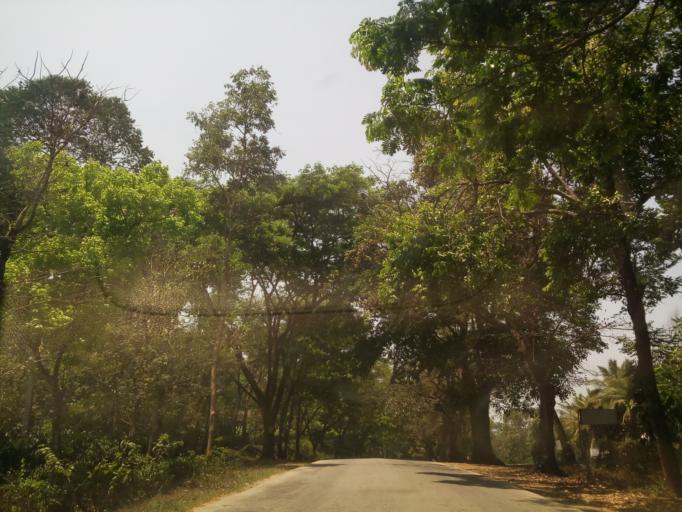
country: IN
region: Karnataka
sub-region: Hassan
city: Sakleshpur
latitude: 12.9523
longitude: 75.8223
